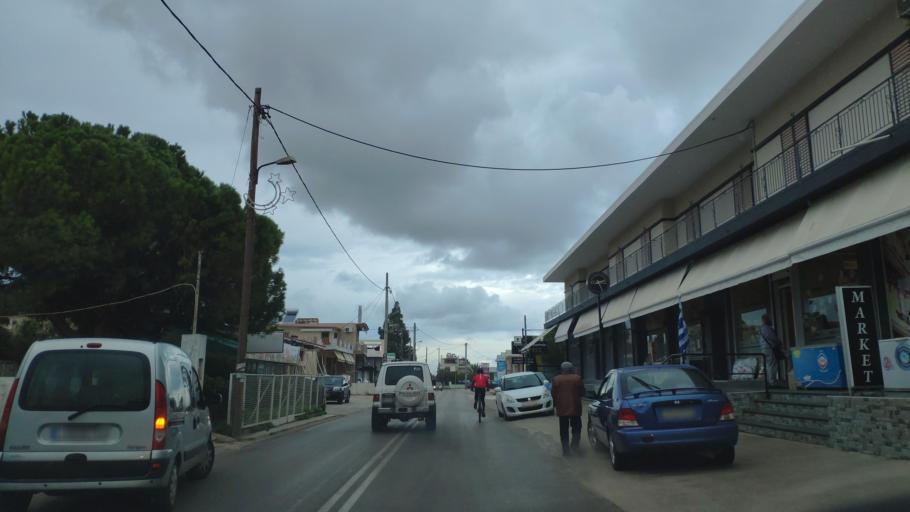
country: GR
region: Attica
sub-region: Nomarchia Anatolikis Attikis
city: Artemida
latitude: 37.9471
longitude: 24.0077
